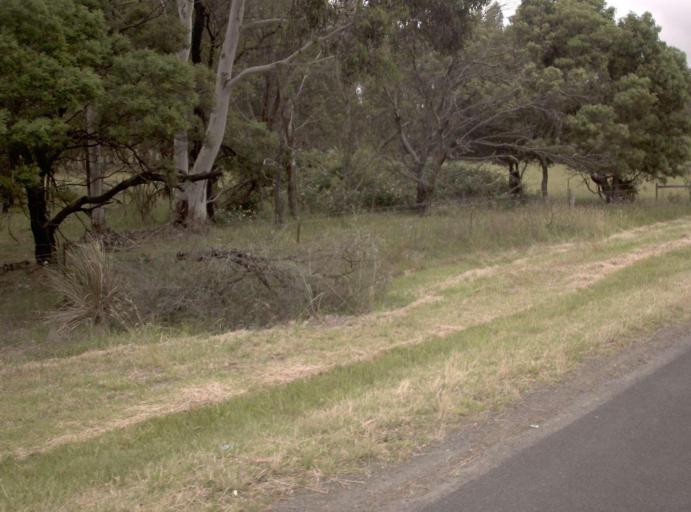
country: AU
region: Victoria
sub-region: Latrobe
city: Morwell
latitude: -38.2715
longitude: 146.4227
